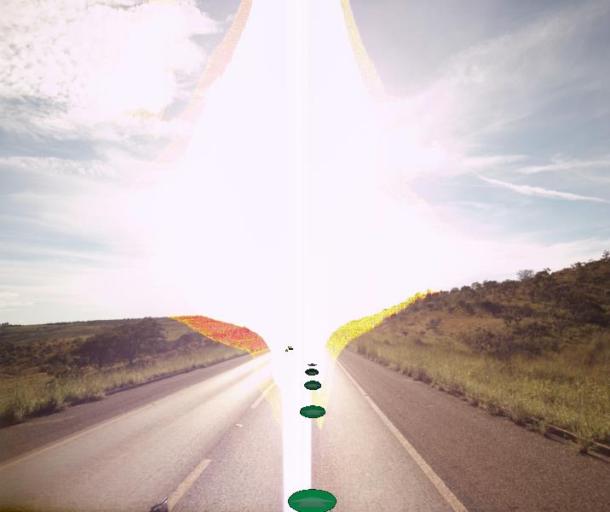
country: BR
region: Federal District
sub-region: Brasilia
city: Brasilia
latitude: -15.7546
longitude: -48.4294
